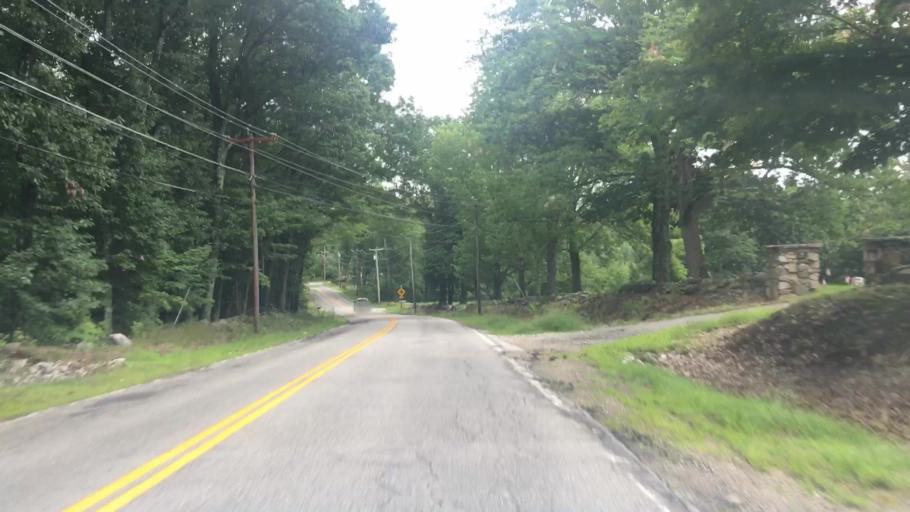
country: US
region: Maine
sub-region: York County
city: Limerick
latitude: 43.6810
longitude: -70.7888
